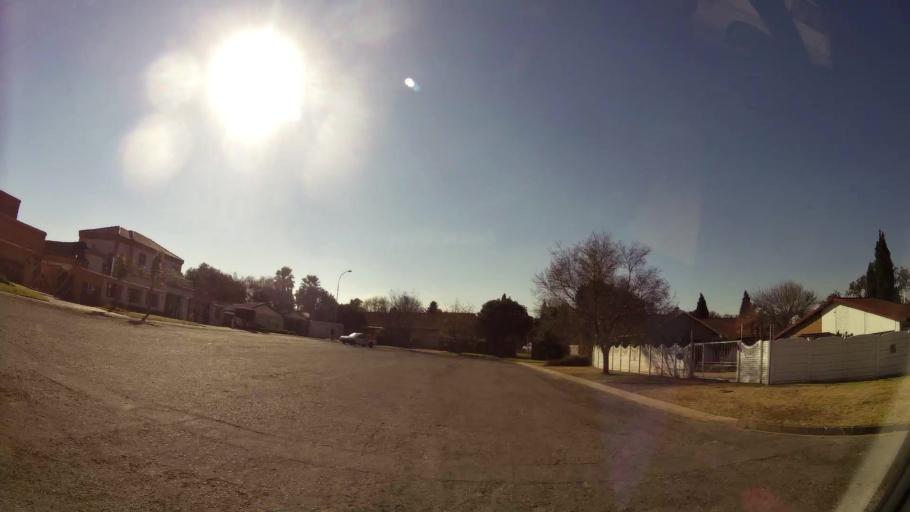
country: ZA
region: Gauteng
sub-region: City of Johannesburg Metropolitan Municipality
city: Johannesburg
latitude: -26.2779
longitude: 28.0302
